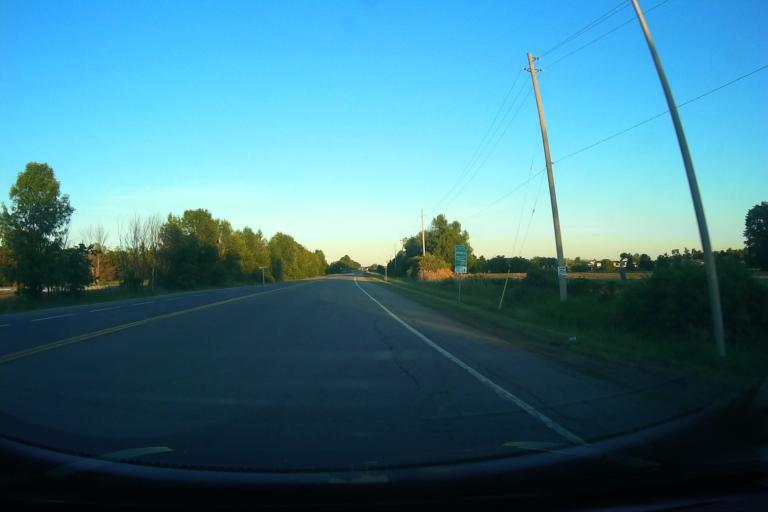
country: CA
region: Ontario
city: Casselman
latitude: 45.1008
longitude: -75.2379
